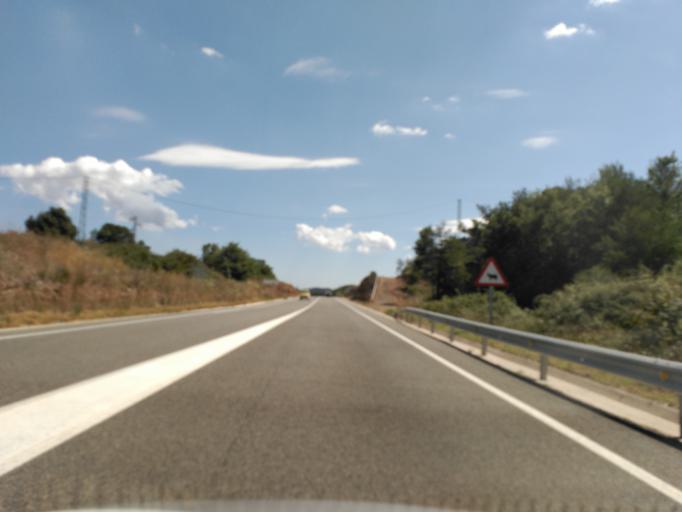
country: ES
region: Catalonia
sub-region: Provincia de Barcelona
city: Olost
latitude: 41.9561
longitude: 2.1358
